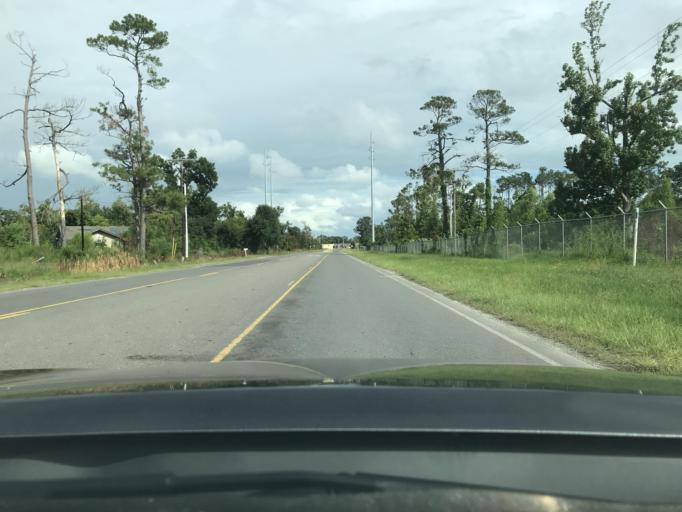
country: US
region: Louisiana
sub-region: Calcasieu Parish
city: Westlake
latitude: 30.2514
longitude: -93.2716
